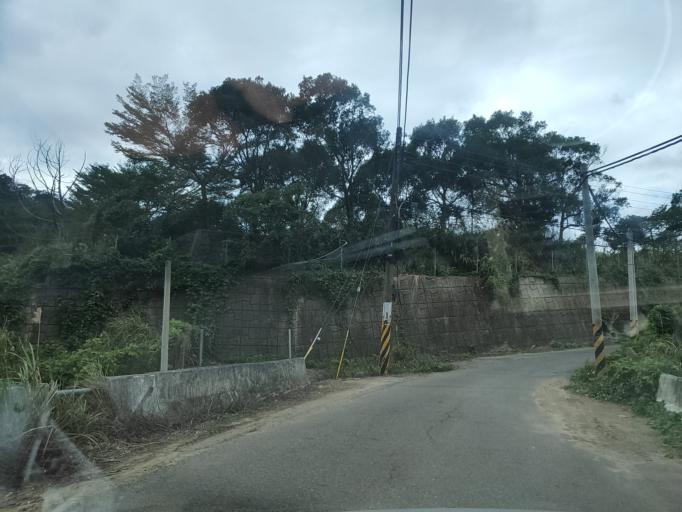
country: TW
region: Taiwan
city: Fengyuan
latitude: 24.3549
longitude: 120.7757
